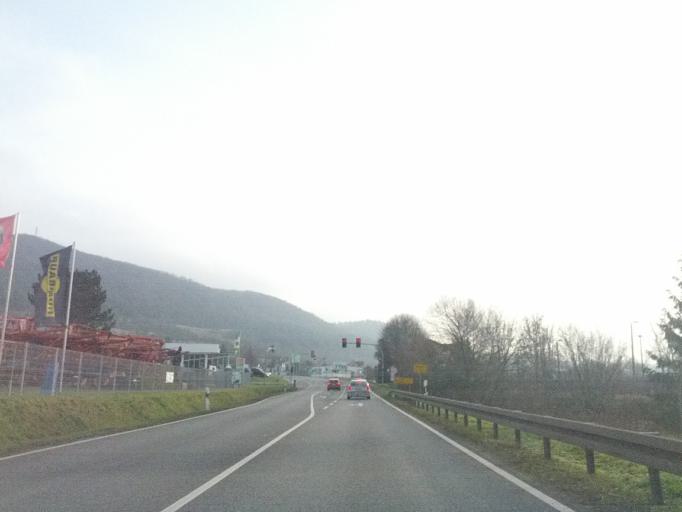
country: DE
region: Thuringia
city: Walldorf
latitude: 50.6186
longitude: 10.3892
